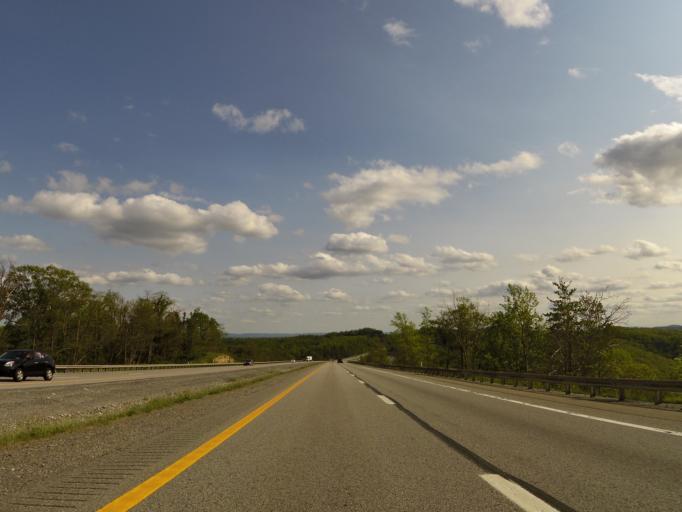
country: US
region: West Virginia
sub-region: Raleigh County
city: Shady Spring
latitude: 37.5600
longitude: -81.1134
